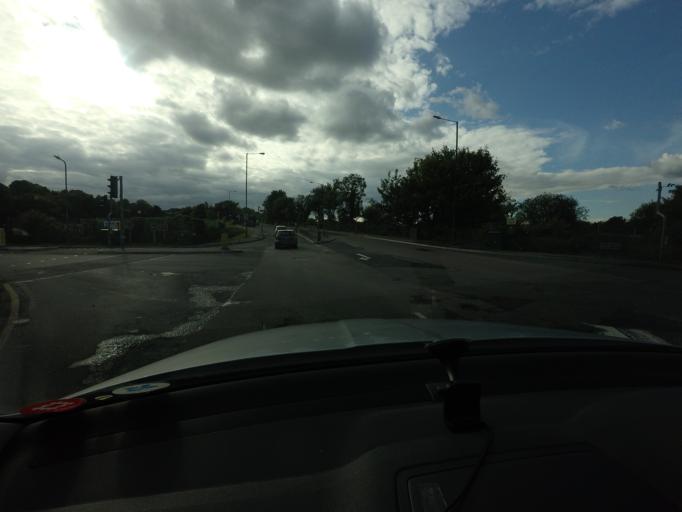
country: GB
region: England
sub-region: Kent
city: Swanscombe
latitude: 51.4512
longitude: 0.2999
